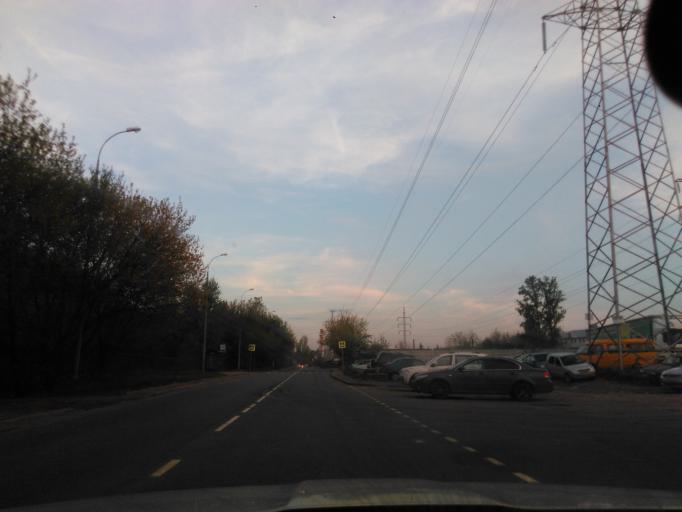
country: RU
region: Moscow
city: Kapotnya
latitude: 55.6629
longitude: 37.8095
